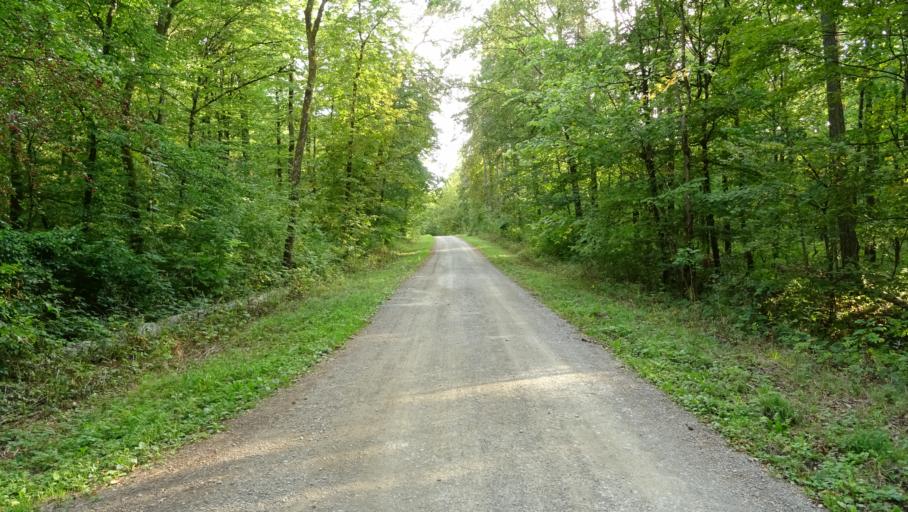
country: DE
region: Baden-Wuerttemberg
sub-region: Karlsruhe Region
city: Mosbach
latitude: 49.3794
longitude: 9.1319
